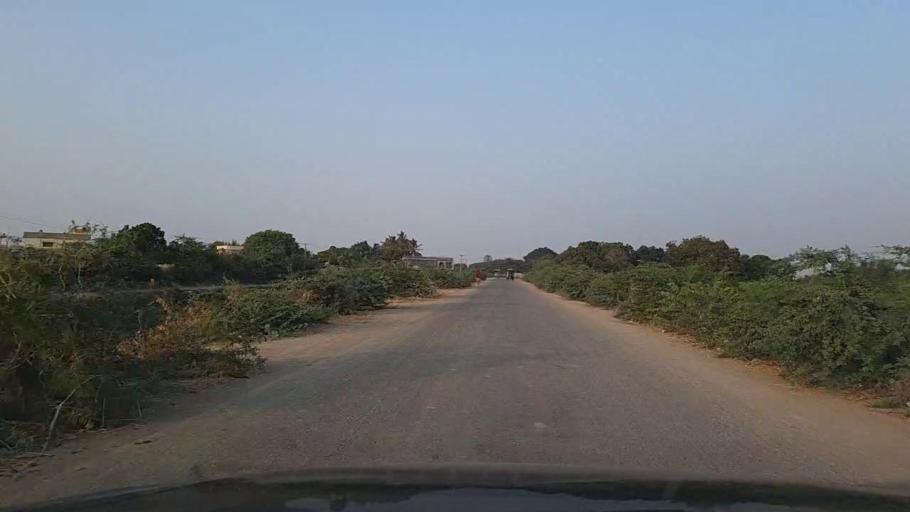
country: PK
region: Sindh
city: Mirpur Sakro
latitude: 24.5487
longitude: 67.8384
